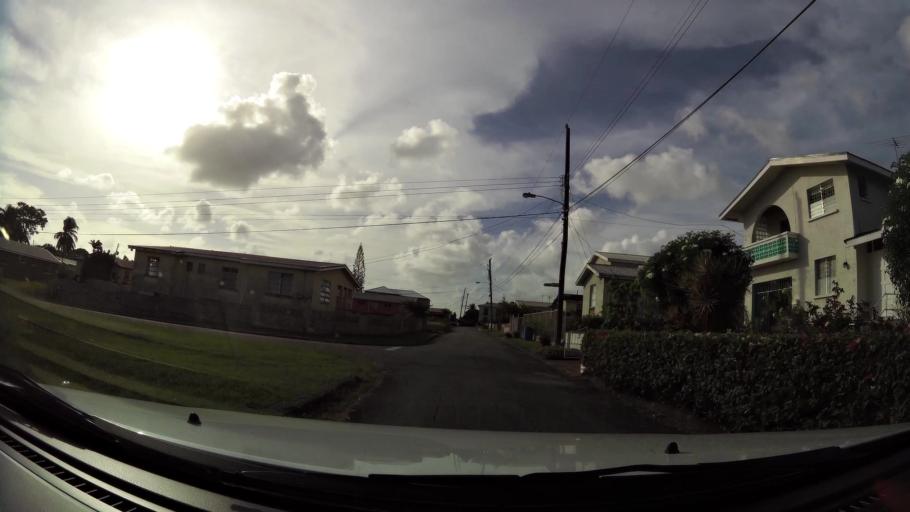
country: BB
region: Christ Church
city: Oistins
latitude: 13.0805
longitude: -59.5674
